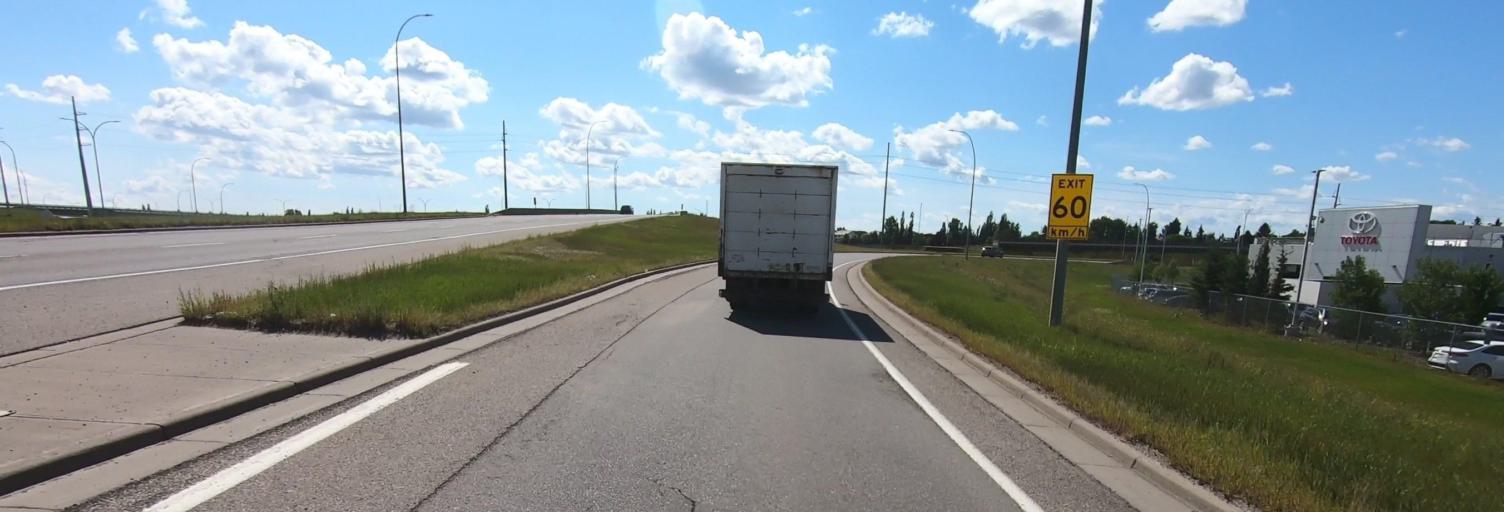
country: CA
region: Alberta
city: Calgary
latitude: 50.9472
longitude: -113.9819
